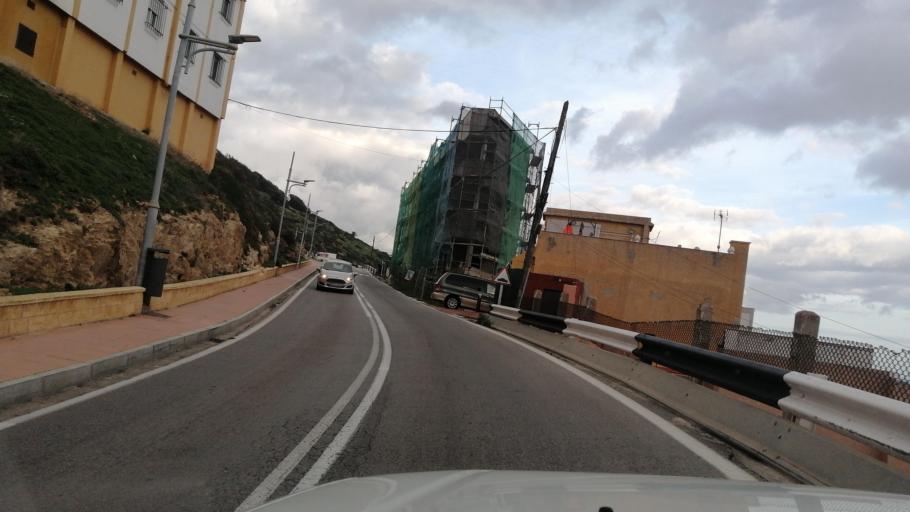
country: ES
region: Ceuta
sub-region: Ceuta
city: Ceuta
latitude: 35.8901
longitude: -5.2932
